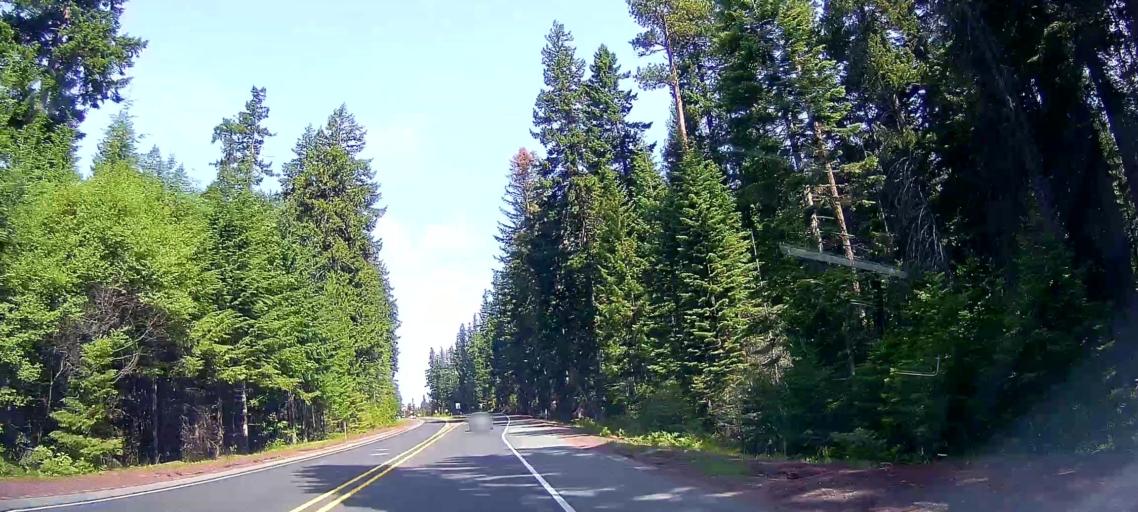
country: US
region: Oregon
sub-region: Clackamas County
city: Mount Hood Village
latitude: 45.1283
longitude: -121.5967
